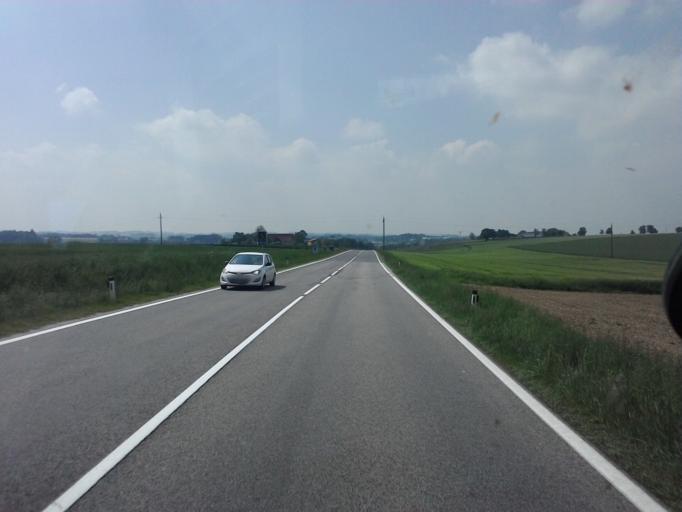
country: AT
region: Upper Austria
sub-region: Politischer Bezirk Steyr-Land
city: Waldneukirchen
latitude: 48.0250
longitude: 14.2513
